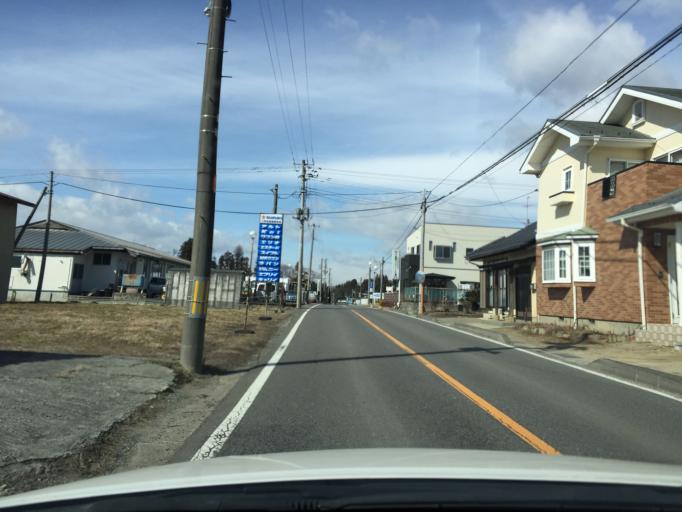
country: JP
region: Fukushima
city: Funehikimachi-funehiki
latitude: 37.3986
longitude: 140.5674
